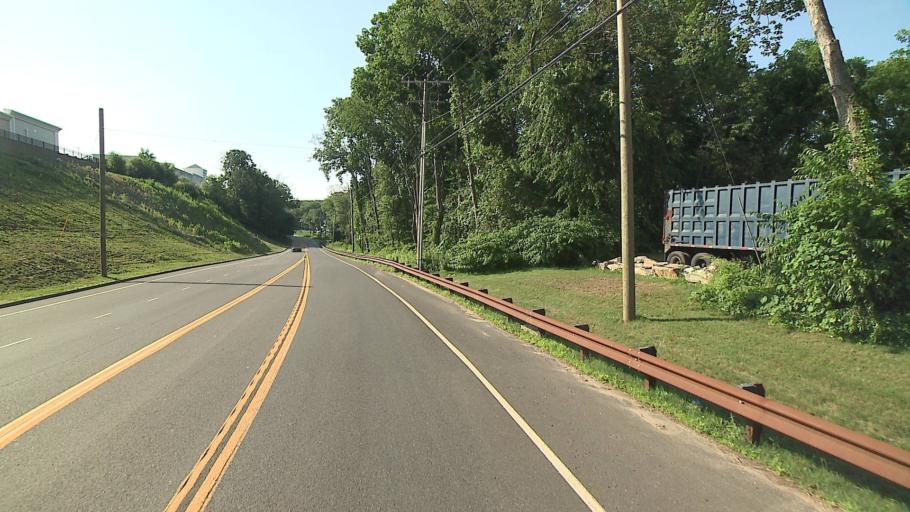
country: US
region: Connecticut
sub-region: New Haven County
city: Guilford
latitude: 41.3002
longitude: -72.7084
